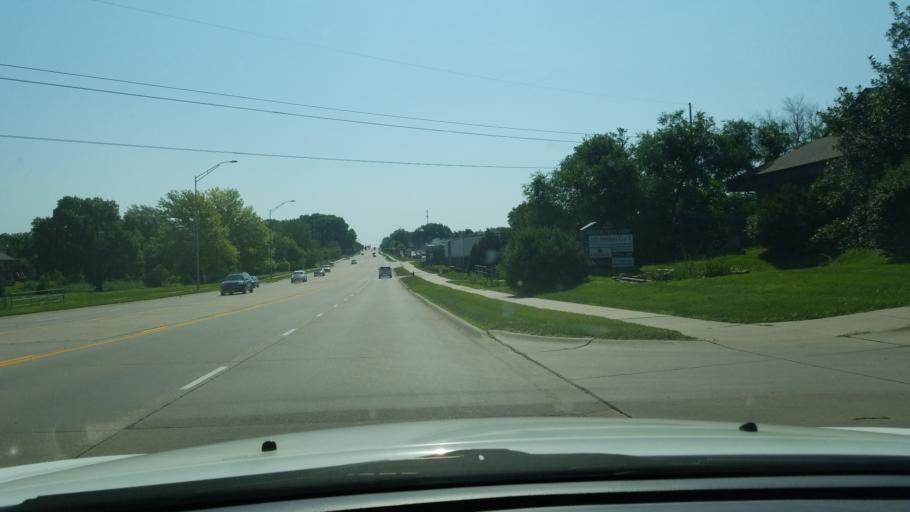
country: US
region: Nebraska
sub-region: Lancaster County
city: Lincoln
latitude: 40.7694
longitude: -96.6192
